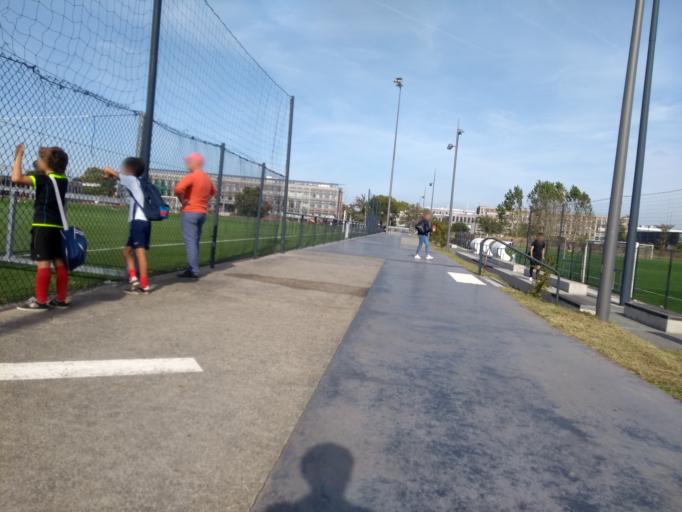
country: FR
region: Aquitaine
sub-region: Departement de la Gironde
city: Talence
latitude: 44.8020
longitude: -0.6058
